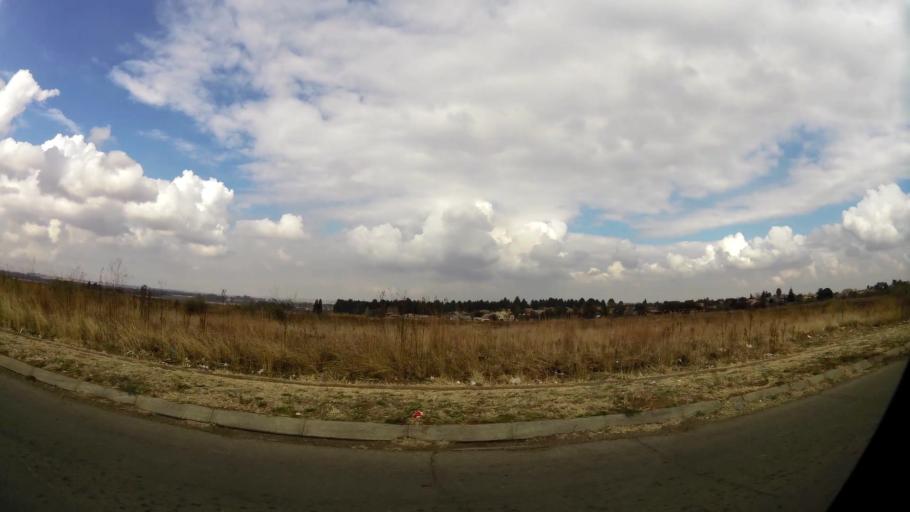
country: ZA
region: Gauteng
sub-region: Sedibeng District Municipality
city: Vanderbijlpark
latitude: -26.7292
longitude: 27.8660
